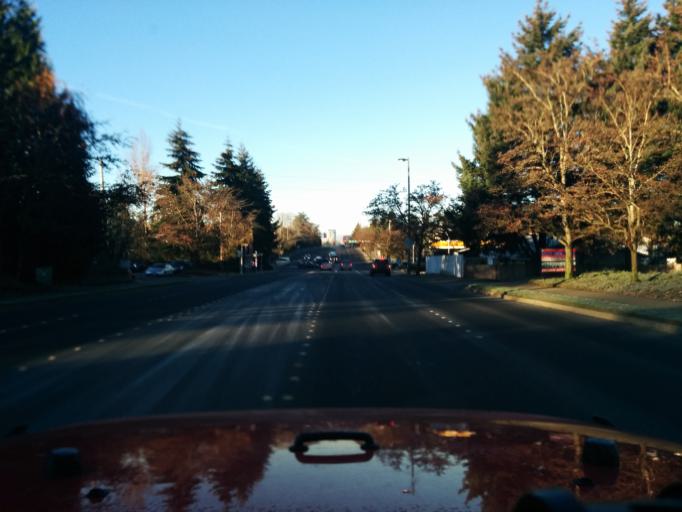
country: US
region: Washington
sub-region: King County
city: Eastgate
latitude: 47.6172
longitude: -122.1518
